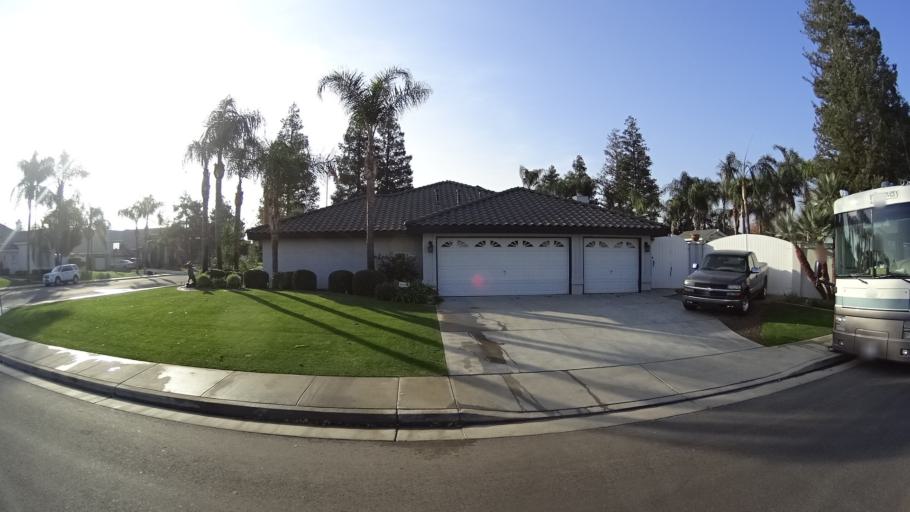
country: US
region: California
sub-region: Kern County
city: Rosedale
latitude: 35.3721
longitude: -119.1403
